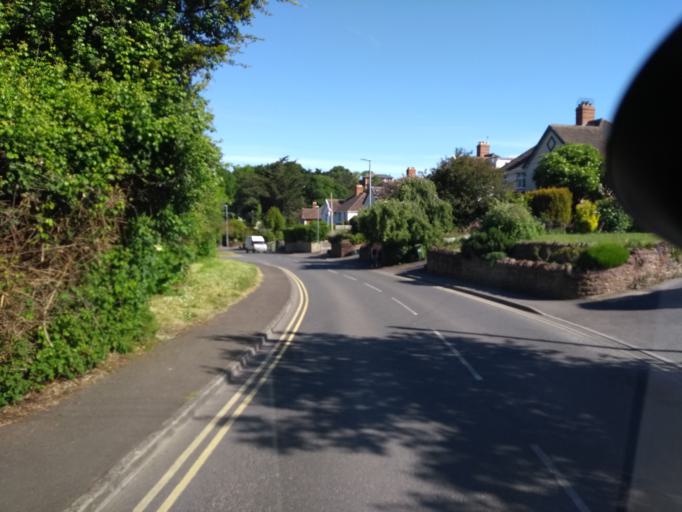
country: GB
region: England
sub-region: Somerset
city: Bridgwater
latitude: 51.1330
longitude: -3.0226
